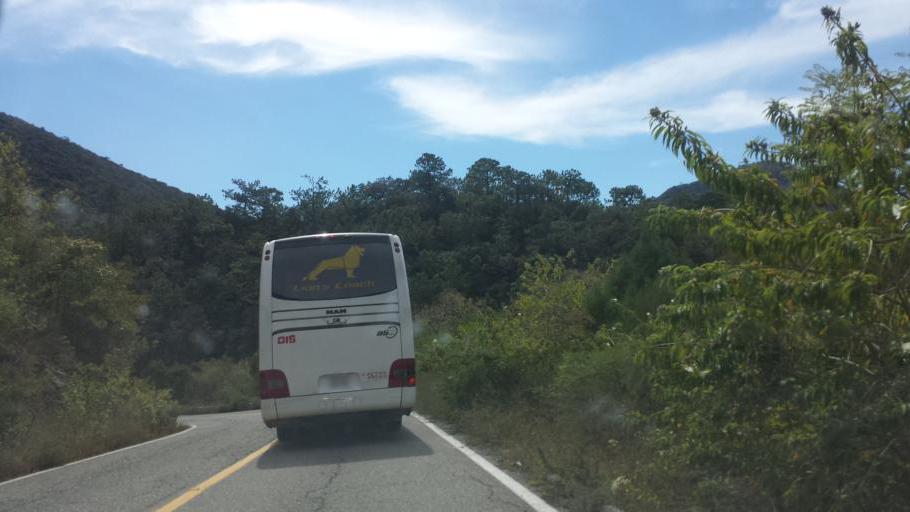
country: MX
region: Oaxaca
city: San Francisco Sola
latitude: 16.4627
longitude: -97.0256
